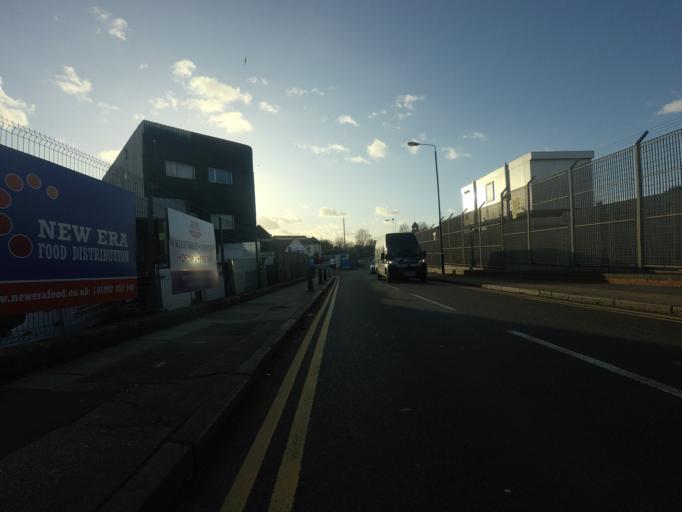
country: GB
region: England
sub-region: Greater London
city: Poplar
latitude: 51.5317
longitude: 0.0029
